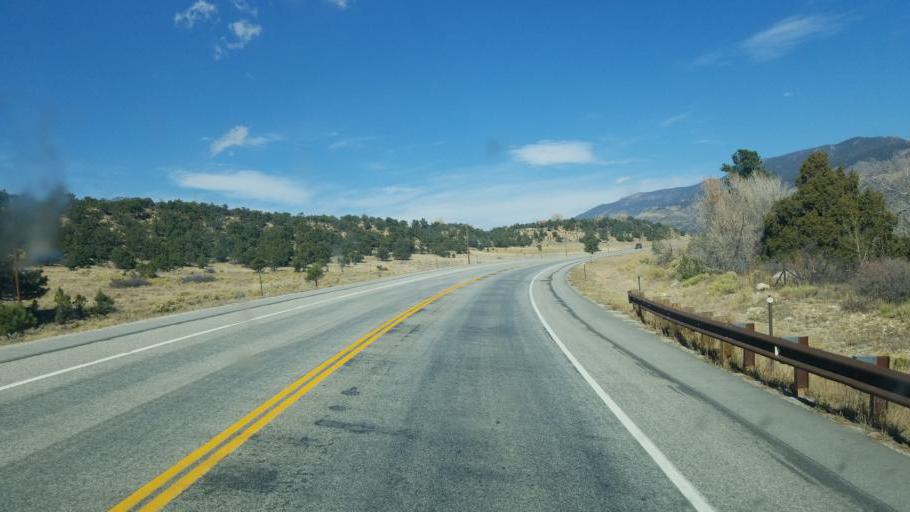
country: US
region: Colorado
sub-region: Chaffee County
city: Buena Vista
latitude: 38.8941
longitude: -106.1734
